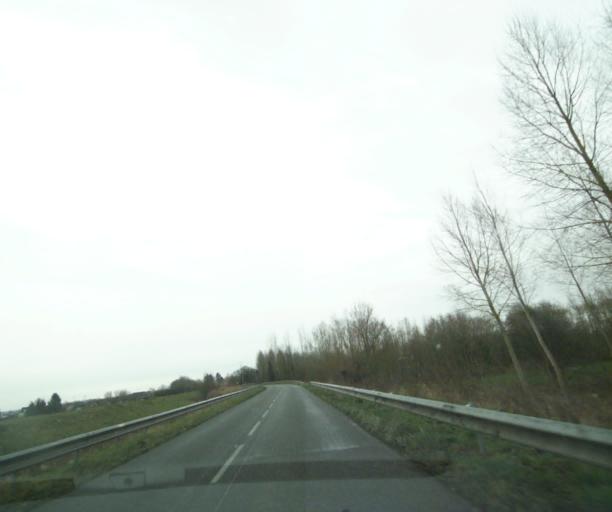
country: FR
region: Nord-Pas-de-Calais
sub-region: Departement du Nord
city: Crespin
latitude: 50.4289
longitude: 3.6548
